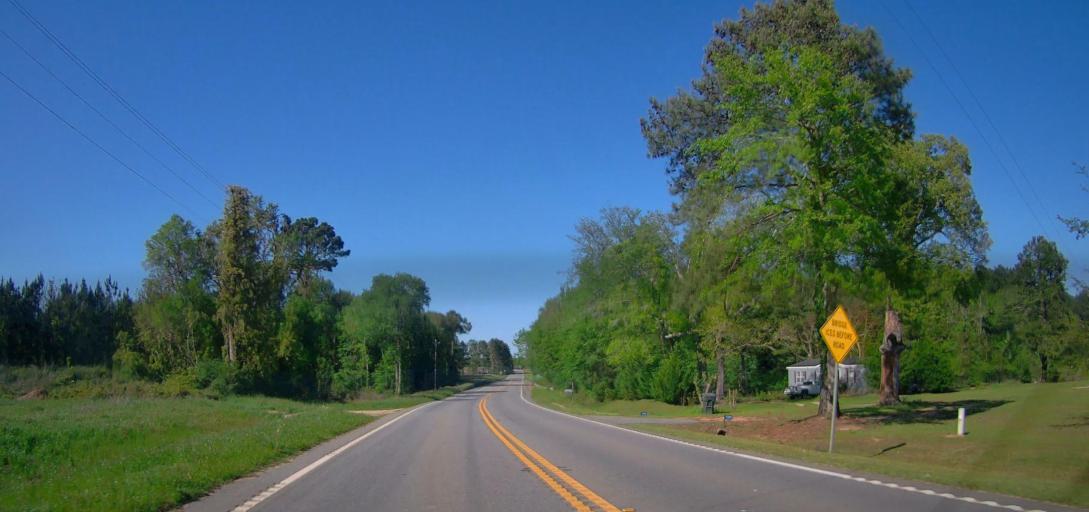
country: US
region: Georgia
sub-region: Pulaski County
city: Hawkinsville
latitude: 32.1514
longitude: -83.5122
